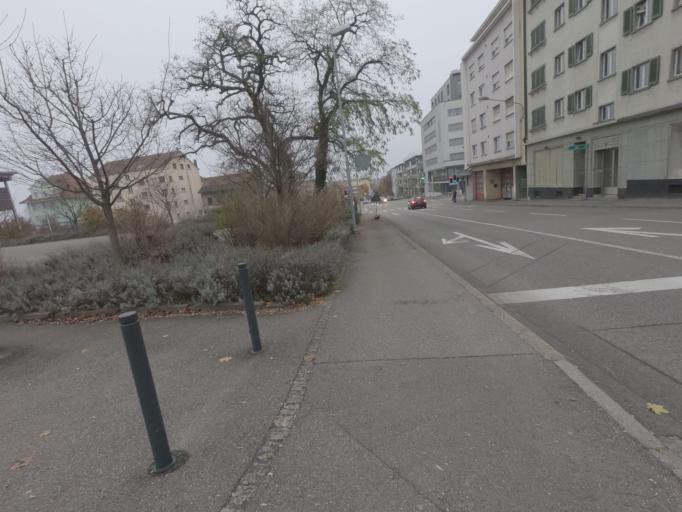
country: CH
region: Solothurn
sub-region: Bezirk Lebern
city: Grenchen
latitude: 47.1934
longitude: 7.3987
